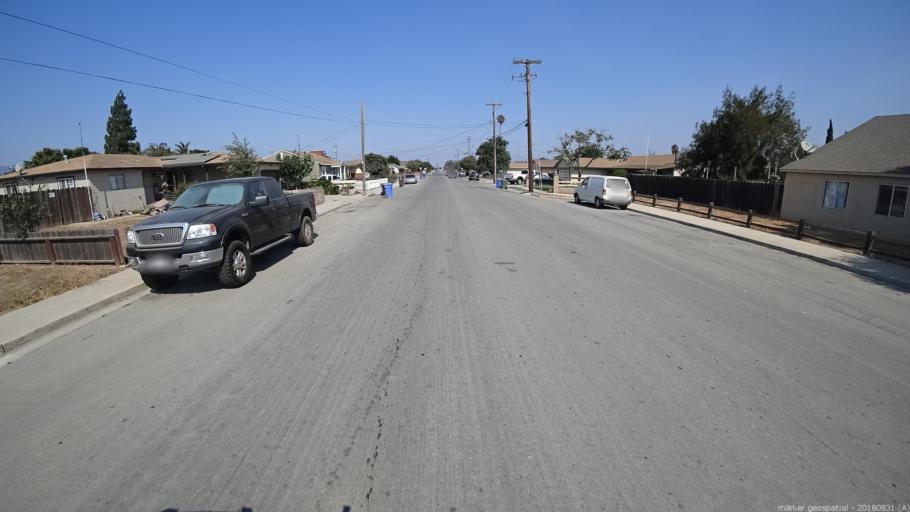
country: US
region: California
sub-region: Monterey County
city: Greenfield
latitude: 36.3251
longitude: -121.2333
